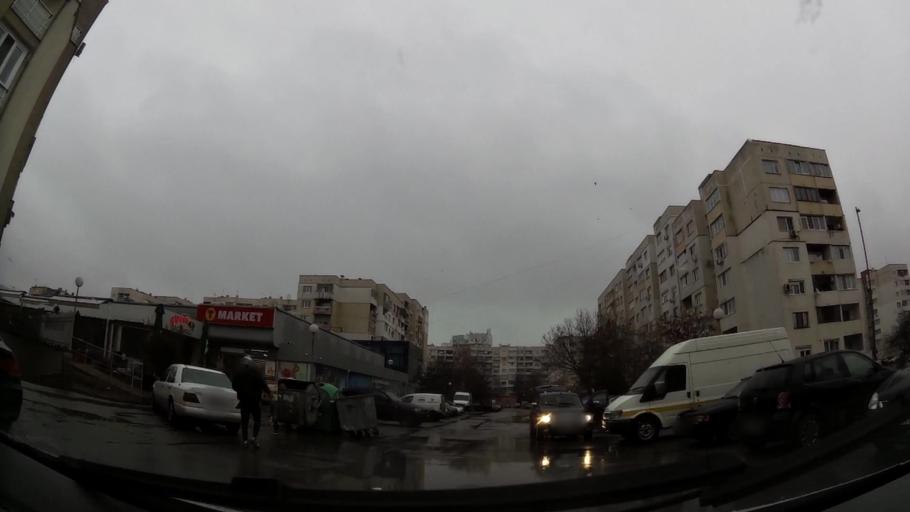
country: BG
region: Sofia-Capital
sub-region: Stolichna Obshtina
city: Sofia
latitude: 42.6470
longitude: 23.4060
